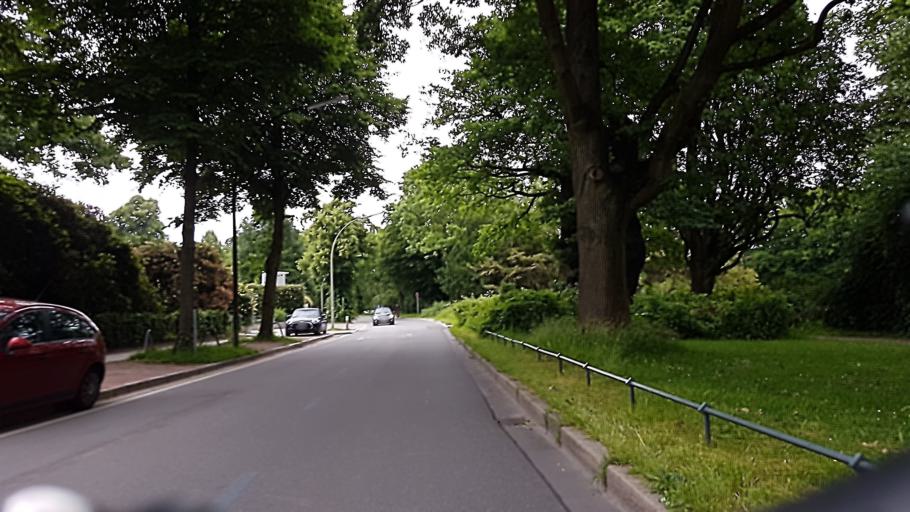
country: DE
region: Hamburg
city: Hamburg
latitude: 53.5761
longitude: 9.9995
